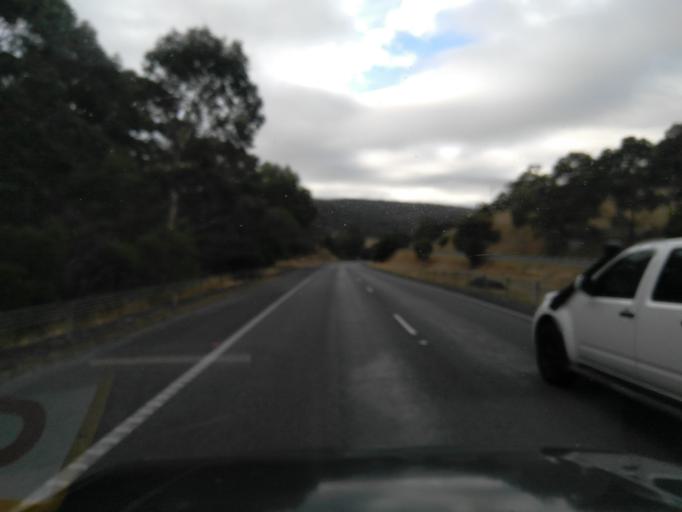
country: AU
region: Tasmania
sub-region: Hobart
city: Dynnyrne
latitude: -42.9308
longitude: 147.3080
